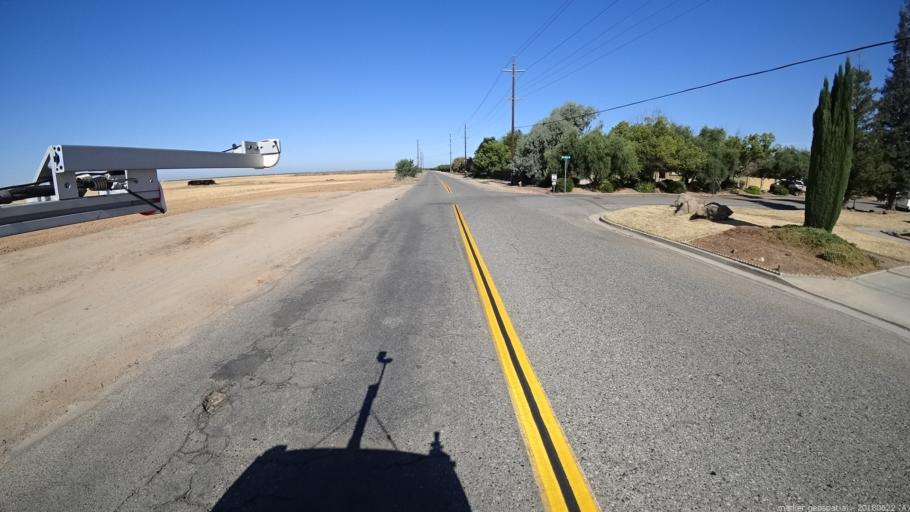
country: US
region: California
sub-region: Madera County
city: Bonadelle Ranchos-Madera Ranchos
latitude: 36.8955
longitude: -119.7978
